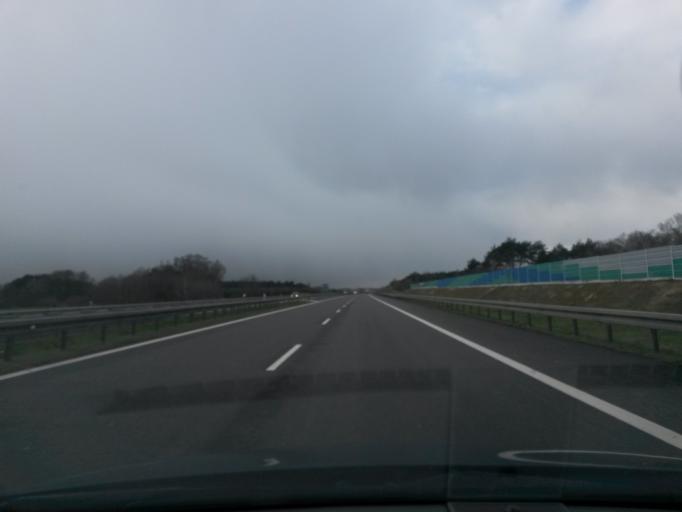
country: PL
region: Greater Poland Voivodeship
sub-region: Powiat koninski
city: Stare Miasto
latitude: 52.1658
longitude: 18.1885
